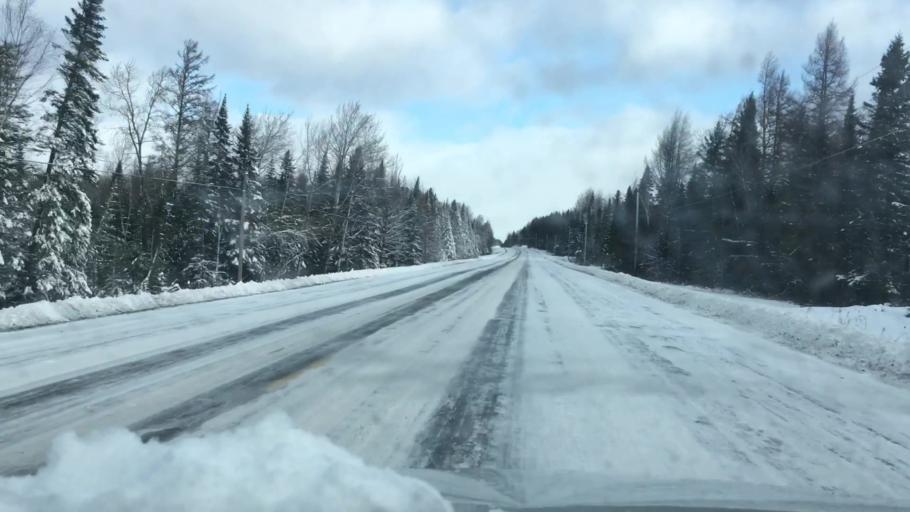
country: US
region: Maine
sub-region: Aroostook County
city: Van Buren
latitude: 47.0308
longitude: -68.0080
